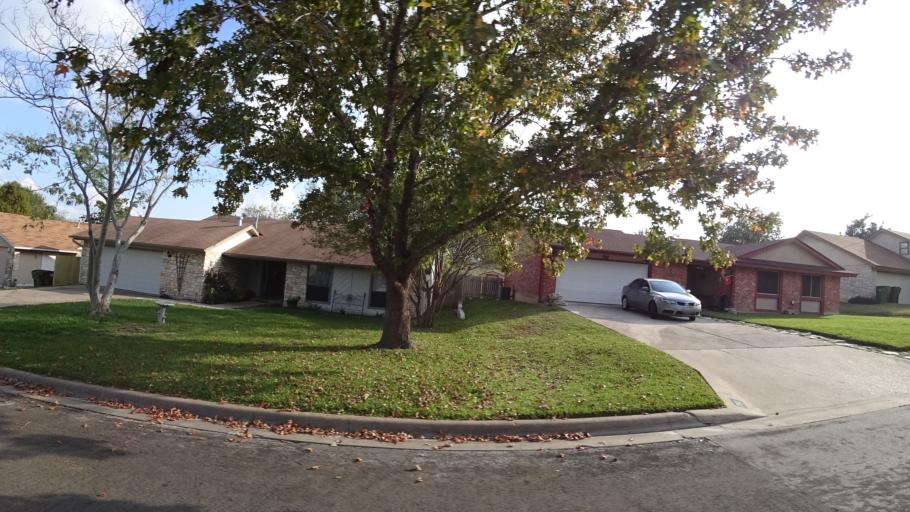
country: US
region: Texas
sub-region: Williamson County
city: Round Rock
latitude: 30.4950
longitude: -97.6687
